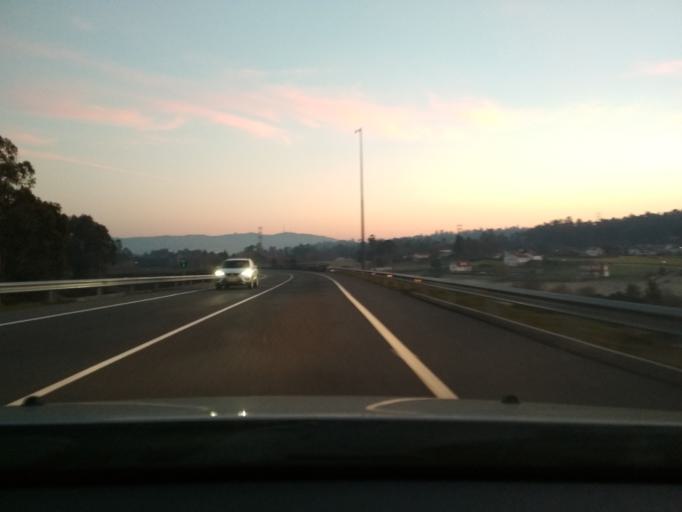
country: ES
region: Galicia
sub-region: Provincia da Coruna
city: Santiago de Compostela
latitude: 42.8443
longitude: -8.5944
